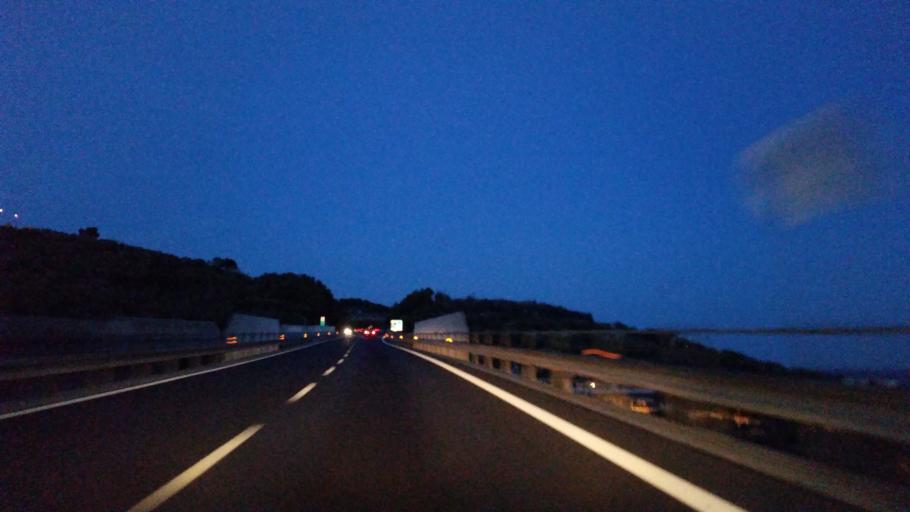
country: IT
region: Liguria
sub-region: Provincia di Imperia
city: Diano Marina
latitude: 43.9226
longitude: 8.0846
